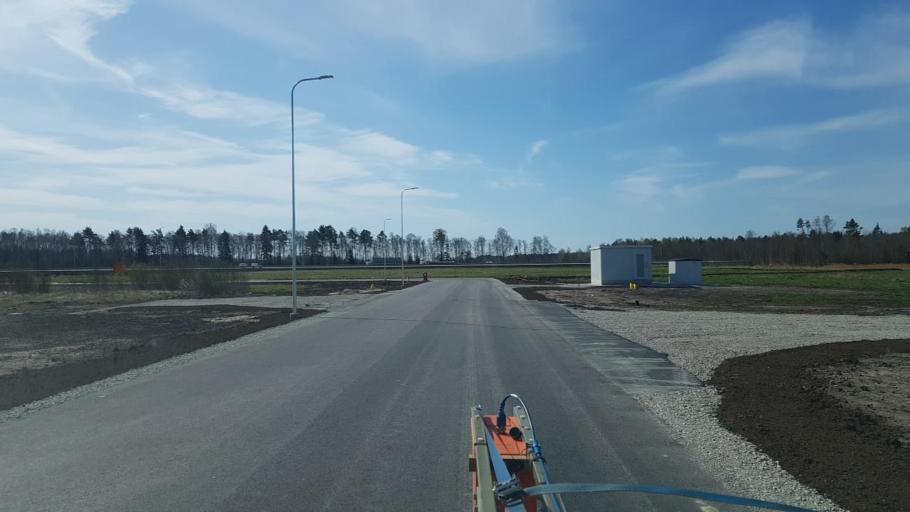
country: EE
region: Harju
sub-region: Kiili vald
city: Kiili
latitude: 59.3351
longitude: 24.7963
